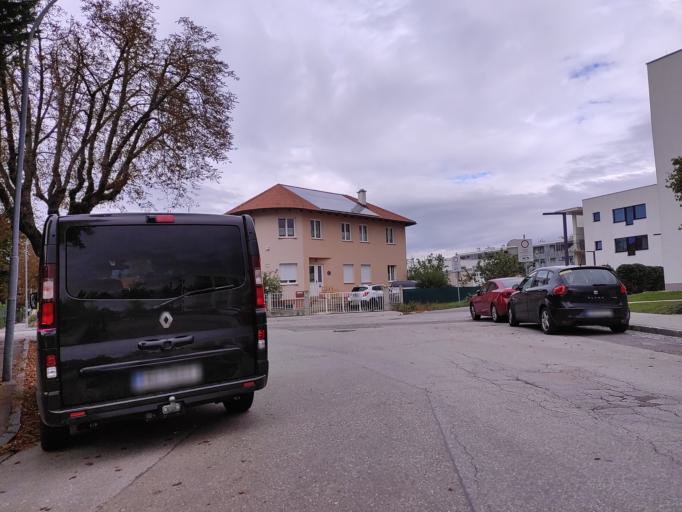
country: AT
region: Lower Austria
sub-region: Politischer Bezirk Baden
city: Baden
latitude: 48.0006
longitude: 16.2517
